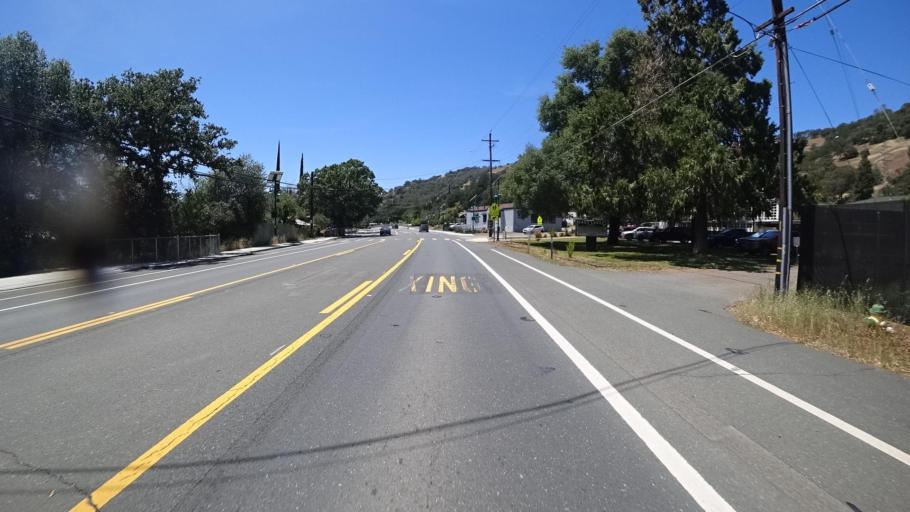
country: US
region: California
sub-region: Lake County
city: Clearlake Oaks
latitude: 39.0277
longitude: -122.6663
